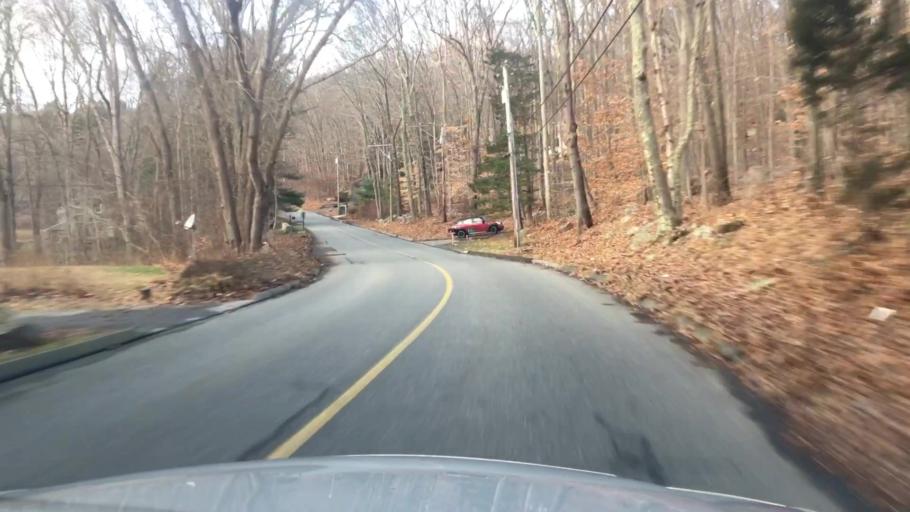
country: US
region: Connecticut
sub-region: Middlesex County
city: Essex Village
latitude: 41.3676
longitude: -72.4014
